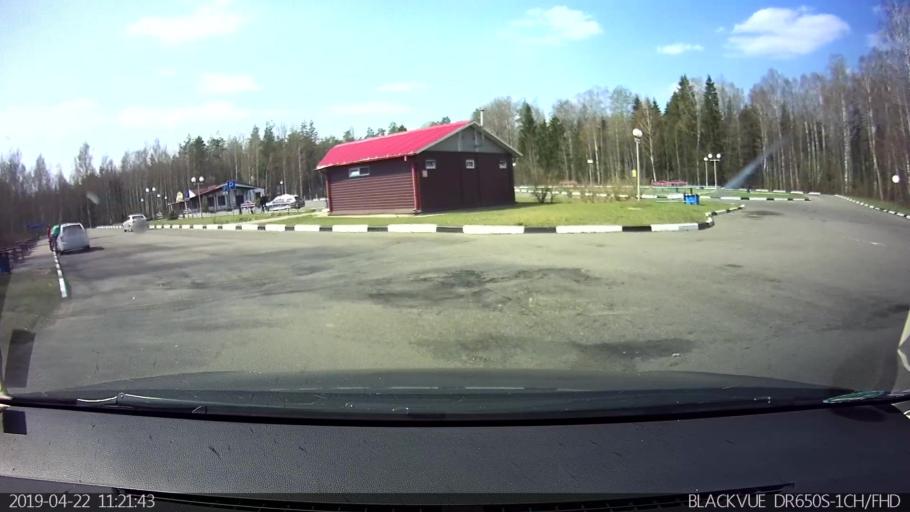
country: BY
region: Minsk
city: Horad Zhodzina
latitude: 54.0718
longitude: 28.4656
